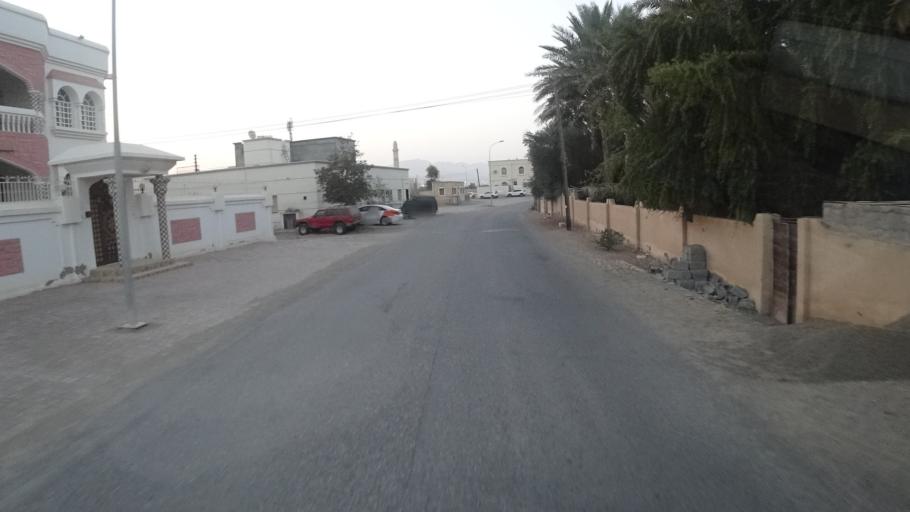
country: OM
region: Ash Sharqiyah
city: Sur
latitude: 22.5426
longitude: 59.4848
